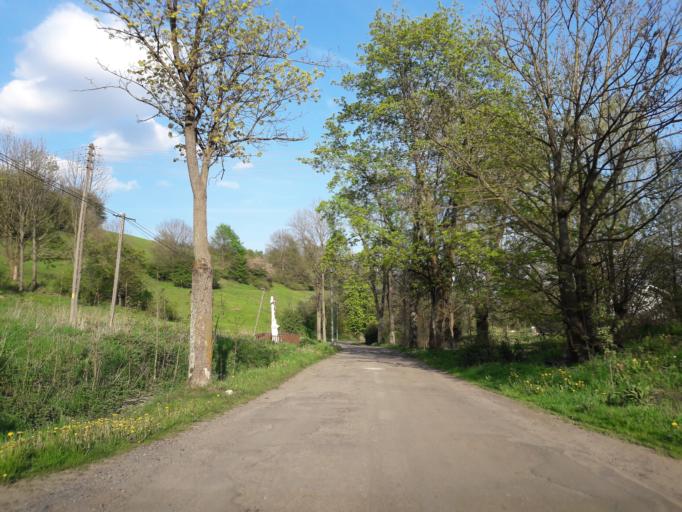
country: PL
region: Lower Silesian Voivodeship
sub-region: Powiat klodzki
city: Duszniki-Zdroj
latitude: 50.4403
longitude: 16.3511
